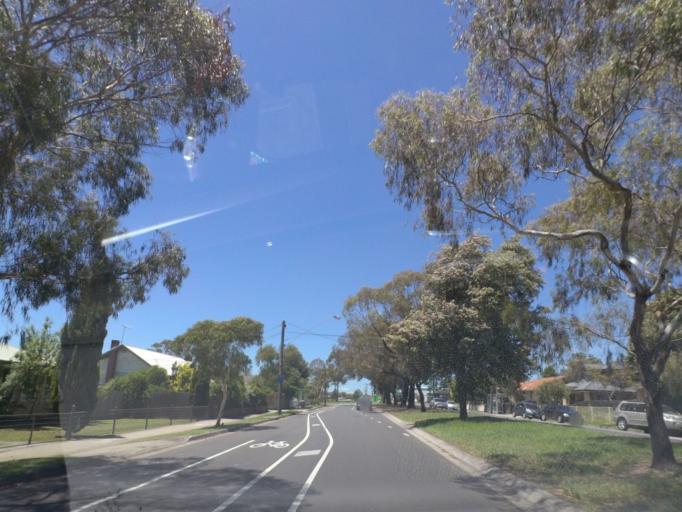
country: AU
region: Victoria
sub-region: Darebin
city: Kingsbury
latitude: -37.7182
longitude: 145.0200
